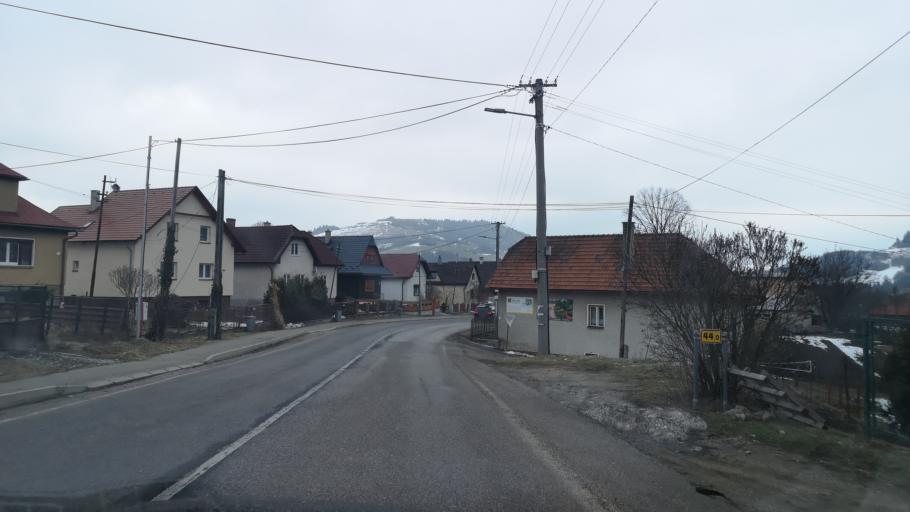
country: SK
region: Zilinsky
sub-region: Okres Dolny Kubin
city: Dolny Kubin
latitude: 49.1949
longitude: 19.1919
